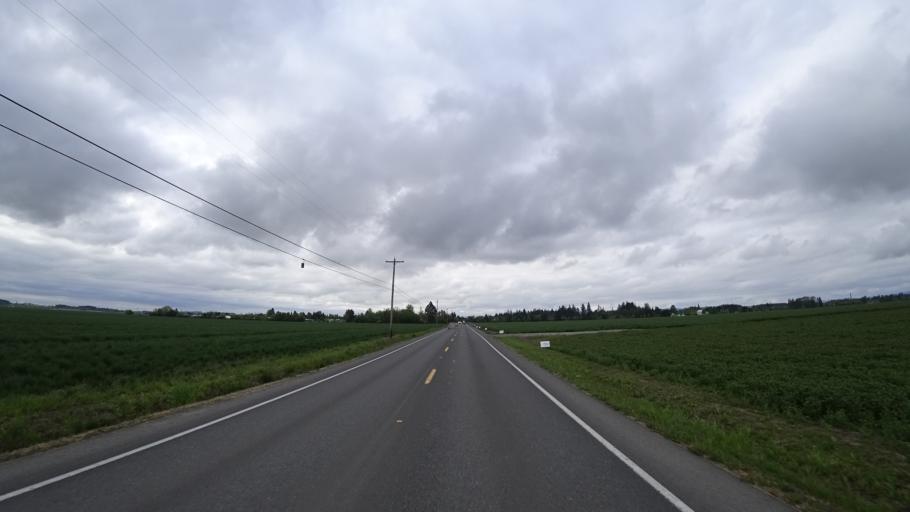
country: US
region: Oregon
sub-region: Washington County
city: Hillsboro
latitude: 45.5564
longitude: -122.9731
